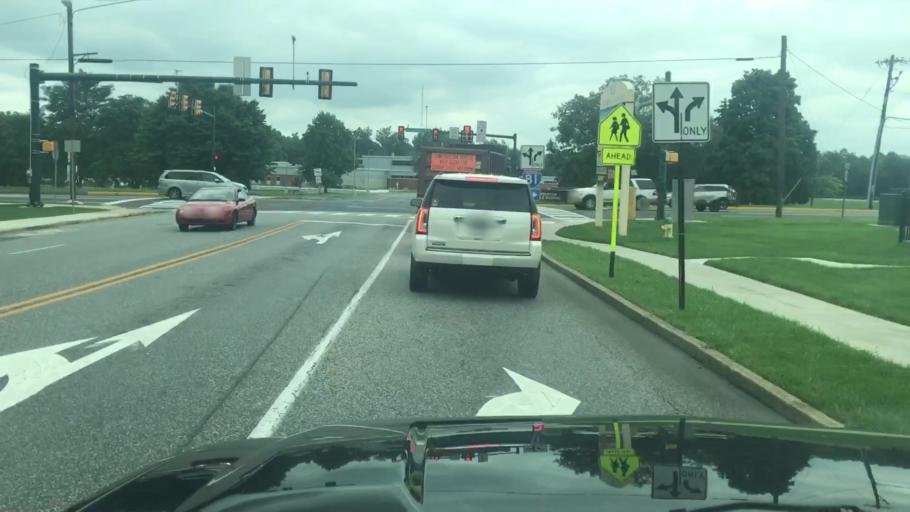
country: US
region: Pennsylvania
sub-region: Cumberland County
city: Carlisle
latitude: 40.1908
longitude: -77.1913
